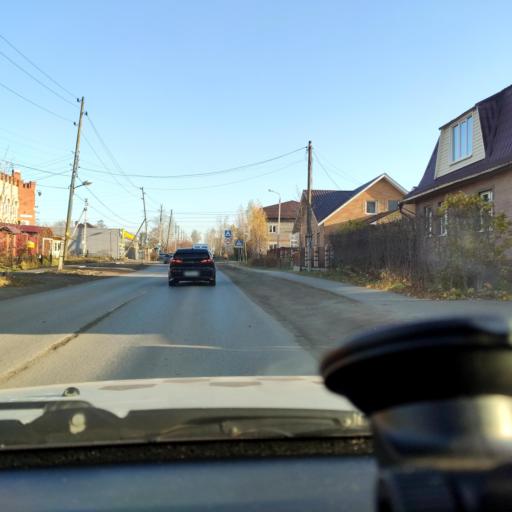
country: RU
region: Perm
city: Perm
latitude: 58.0445
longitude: 56.3285
